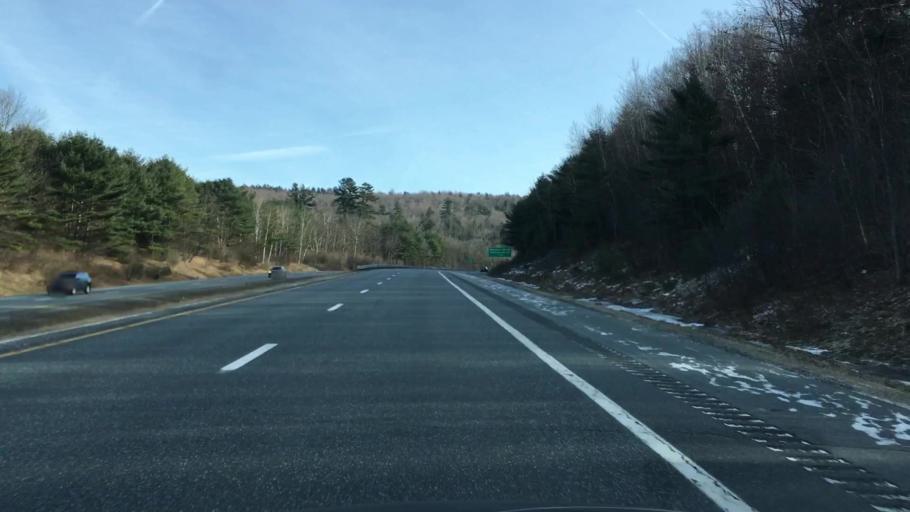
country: US
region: New Hampshire
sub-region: Grafton County
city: Lebanon
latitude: 43.6254
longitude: -72.2041
